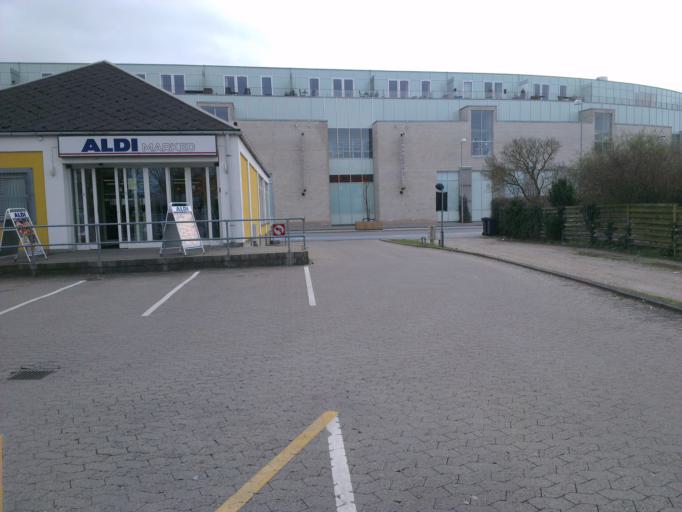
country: PL
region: Lower Silesian Voivodeship
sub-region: Powiat olesnicki
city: Dziadowa Kloda
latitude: 51.2414
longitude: 17.7302
